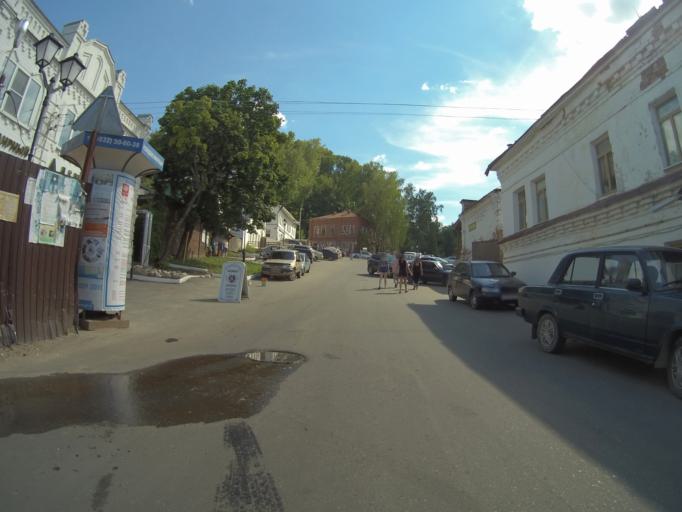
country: RU
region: Ivanovo
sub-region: Privolzhskiy Rayon
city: Ples
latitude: 57.4611
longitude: 41.5129
